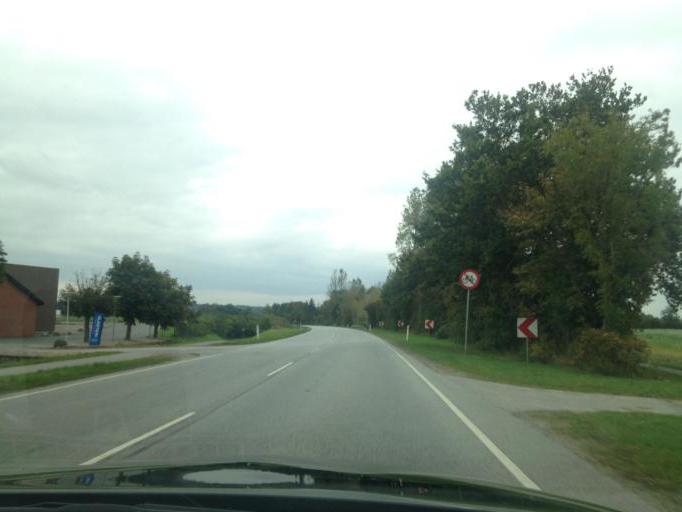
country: DK
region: South Denmark
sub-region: Kolding Kommune
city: Christiansfeld
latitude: 55.3426
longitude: 9.4872
